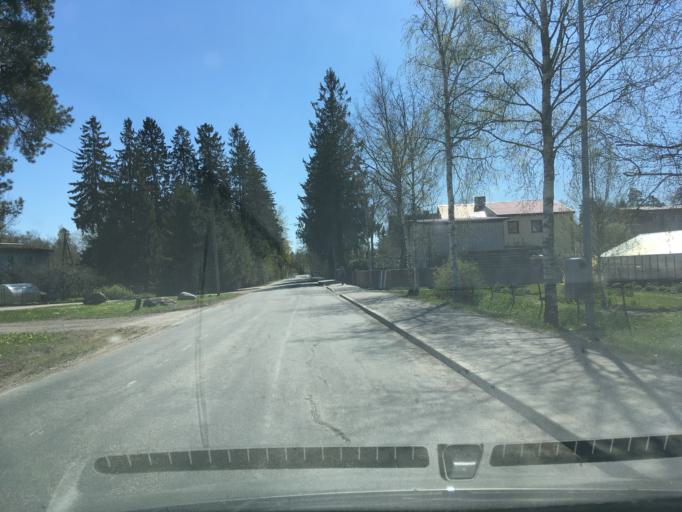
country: EE
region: Harju
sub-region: Raasiku vald
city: Arukula
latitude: 59.3691
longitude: 25.0792
